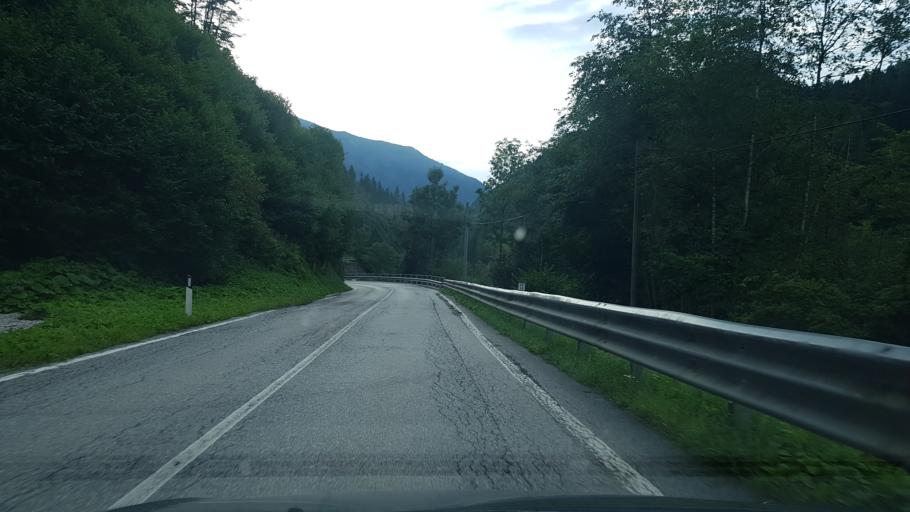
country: IT
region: Friuli Venezia Giulia
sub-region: Provincia di Udine
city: Forni Avoltri
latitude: 46.5726
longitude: 12.8016
